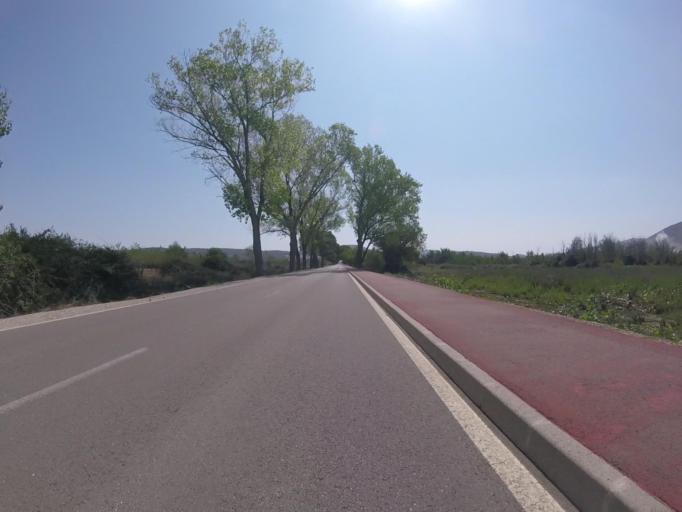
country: ES
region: Valencia
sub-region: Provincia de Castello
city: Cabanes
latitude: 40.1627
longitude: 0.0227
